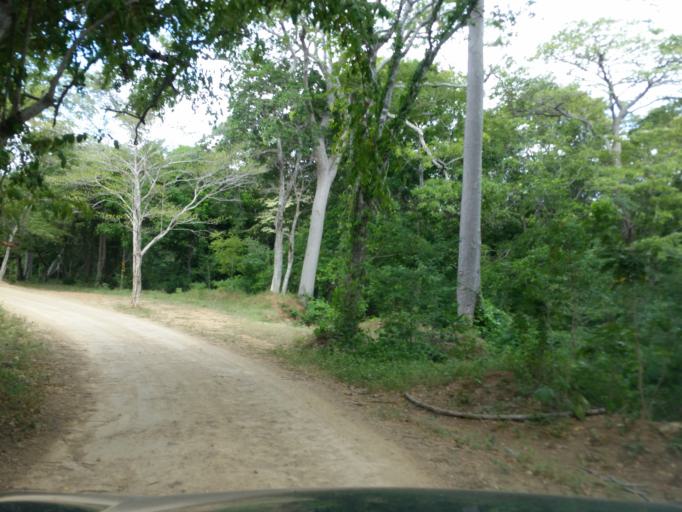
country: NI
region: Rivas
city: San Juan del Sur
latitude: 11.2150
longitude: -85.8395
